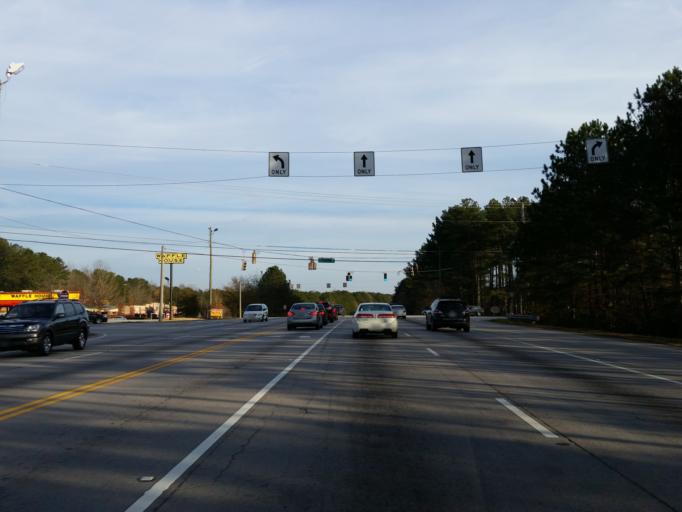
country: US
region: Georgia
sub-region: Cobb County
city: Powder Springs
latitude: 33.8751
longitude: -84.7041
